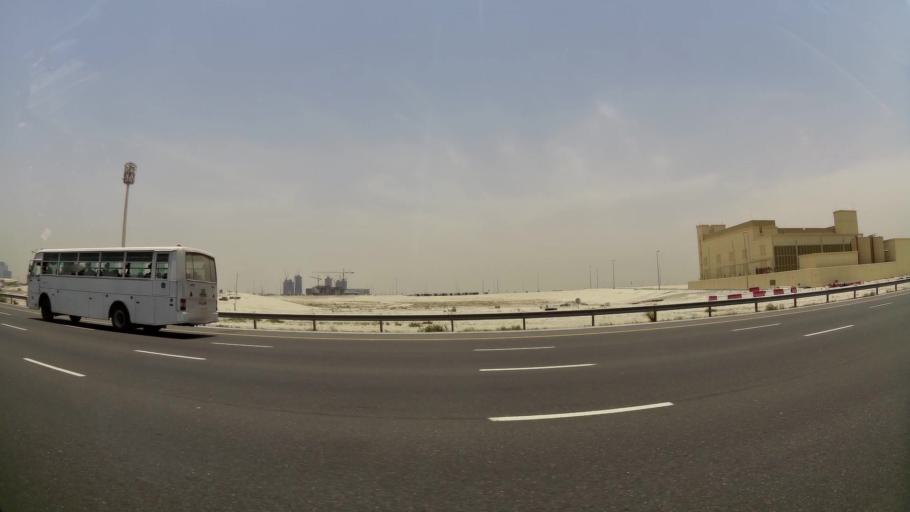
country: AE
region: Ash Shariqah
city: Sharjah
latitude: 25.2127
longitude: 55.3217
